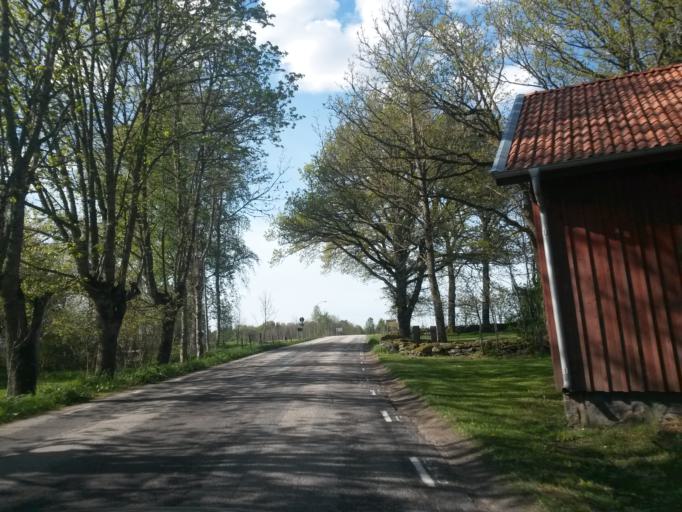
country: SE
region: Vaestra Goetaland
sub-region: Herrljunga Kommun
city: Herrljunga
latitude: 58.0167
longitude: 13.0465
